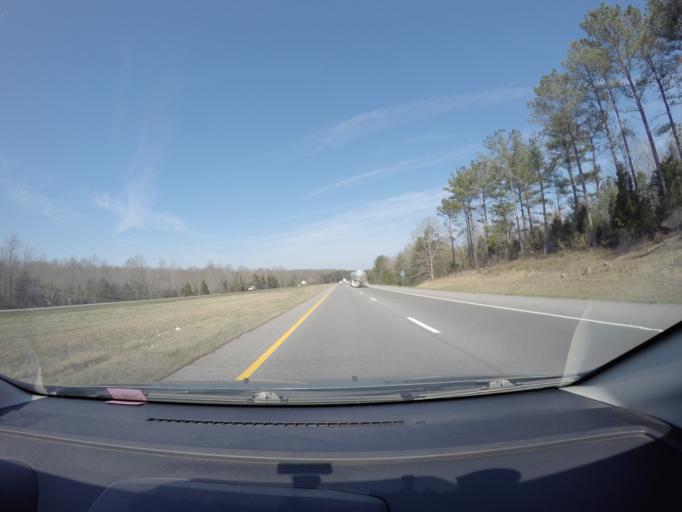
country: US
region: Tennessee
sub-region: Coffee County
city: New Union
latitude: 35.5390
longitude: -86.1719
